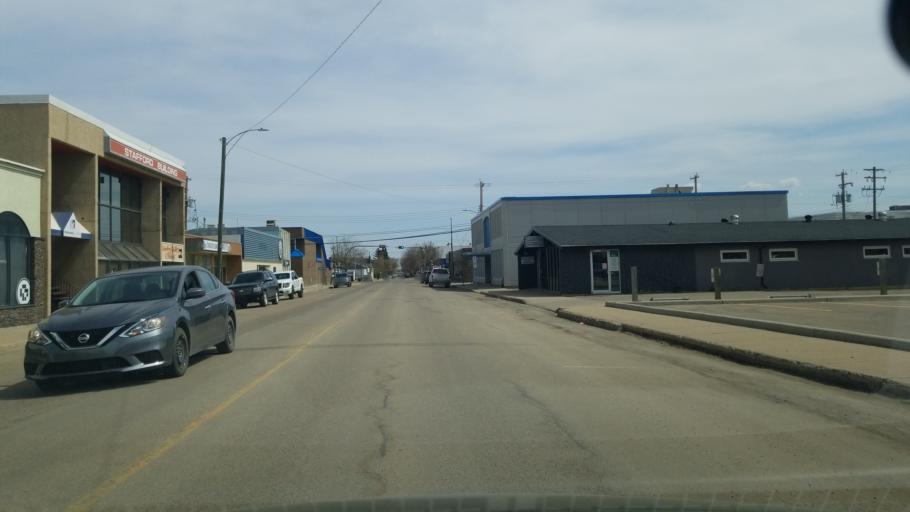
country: CA
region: Saskatchewan
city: Lloydminster
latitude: 53.2816
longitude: -110.0075
